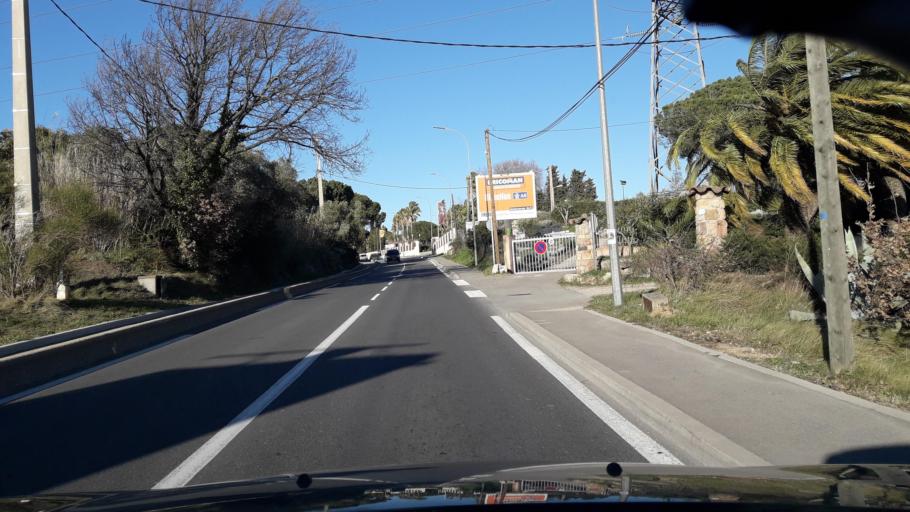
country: FR
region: Provence-Alpes-Cote d'Azur
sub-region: Departement du Var
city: Frejus
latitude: 43.4445
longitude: 6.7258
